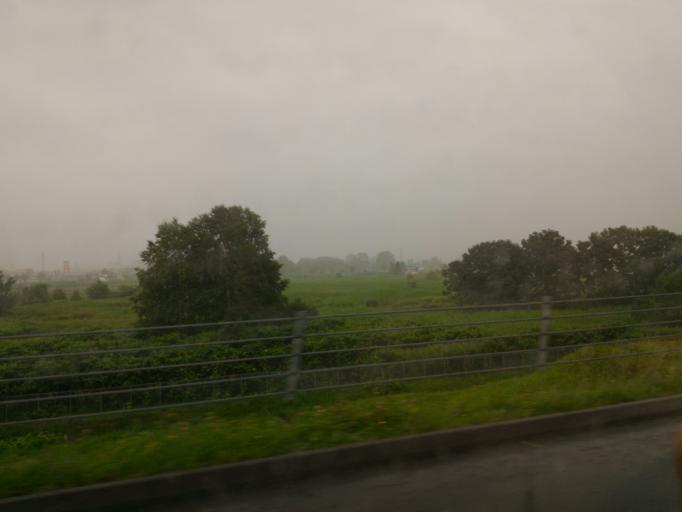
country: JP
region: Hokkaido
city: Nayoro
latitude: 44.3332
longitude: 142.4455
